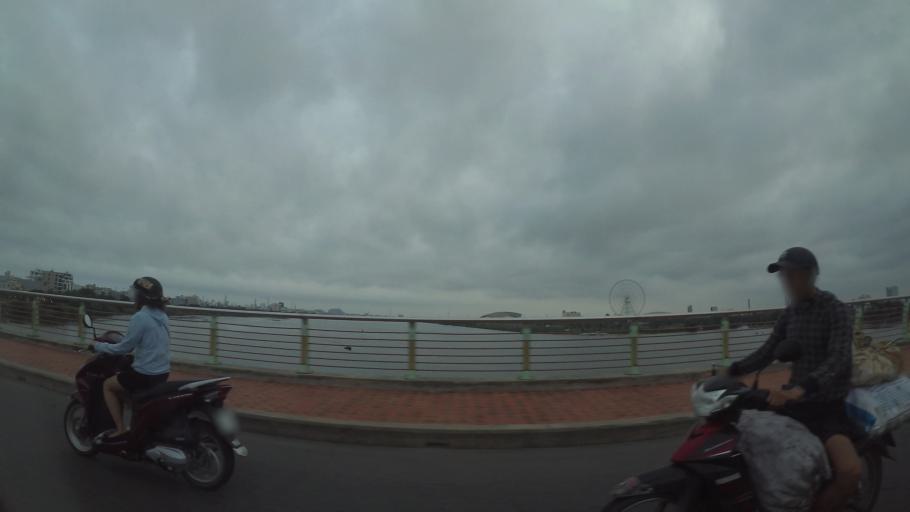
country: VN
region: Da Nang
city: Son Tra
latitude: 16.0504
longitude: 108.2310
